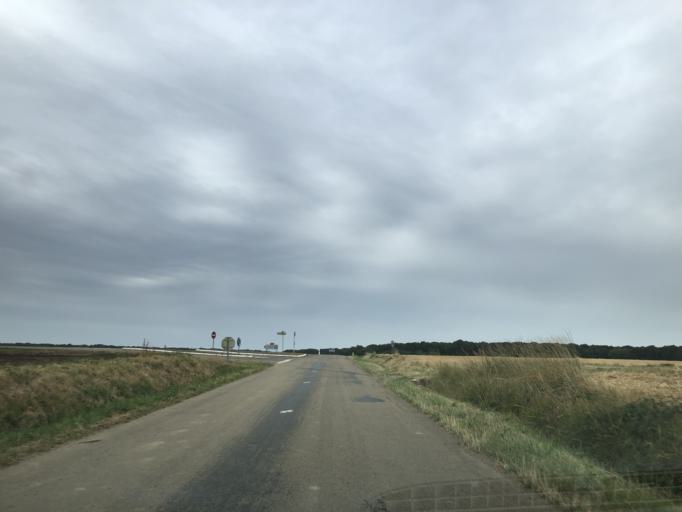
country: FR
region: Centre
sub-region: Departement du Loiret
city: Douchy
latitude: 47.9683
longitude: 3.1447
